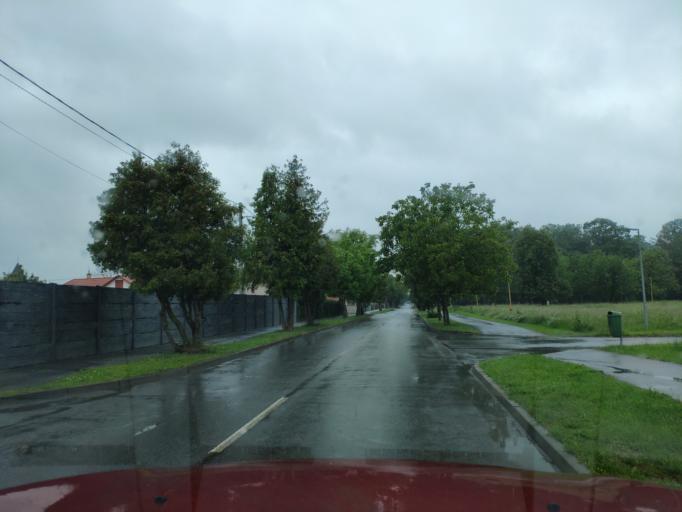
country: SK
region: Kosicky
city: Cierna nad Tisou
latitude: 48.4184
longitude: 22.0924
